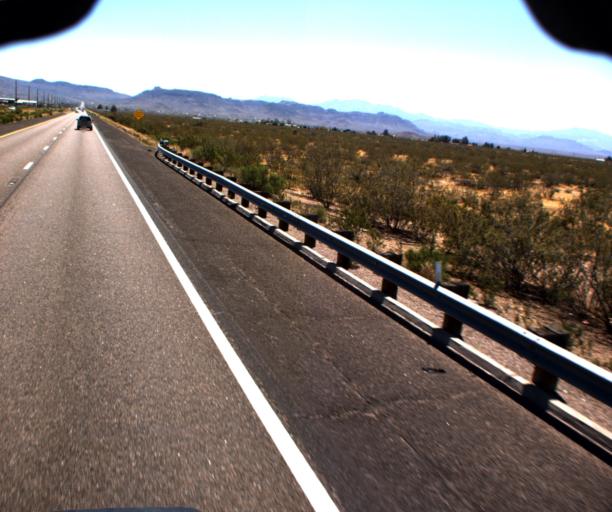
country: US
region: Arizona
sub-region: Mohave County
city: Golden Valley
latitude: 35.2225
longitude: -114.2278
